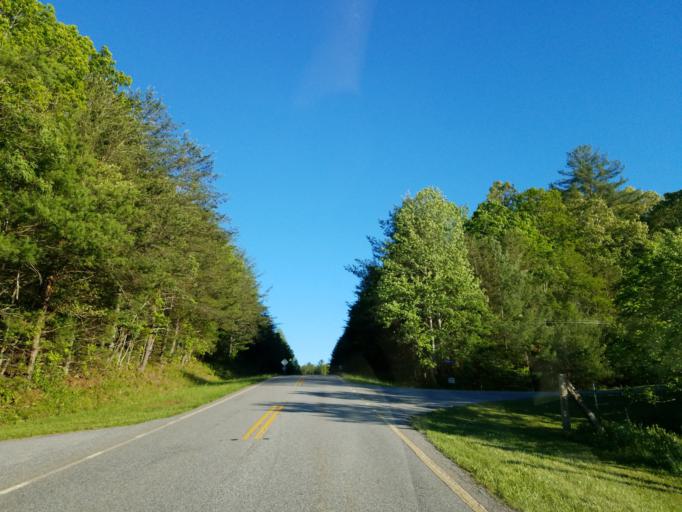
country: US
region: Georgia
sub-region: Fannin County
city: Blue Ridge
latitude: 34.7582
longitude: -84.2397
